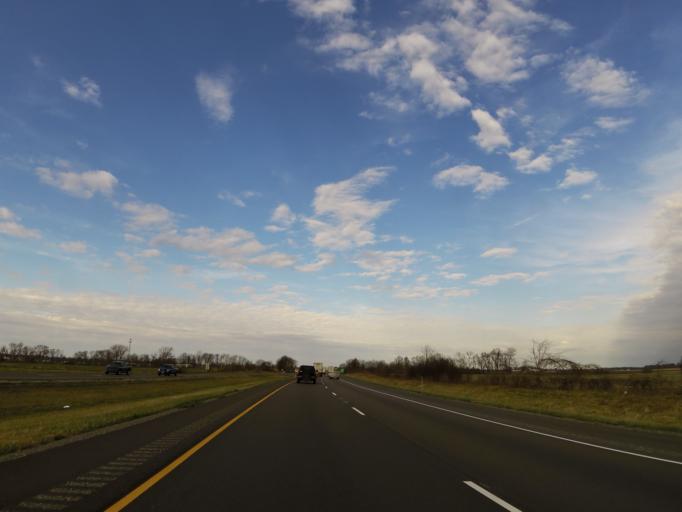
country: US
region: Illinois
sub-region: Washington County
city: Okawville
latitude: 38.4338
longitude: -89.5182
